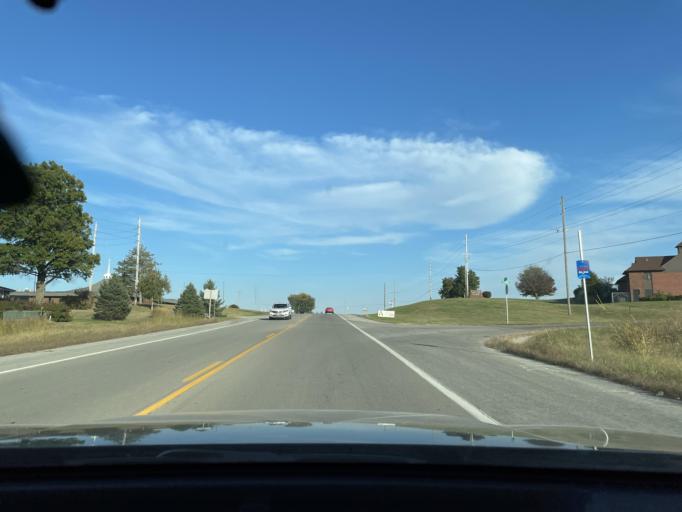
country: US
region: Missouri
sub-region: Buchanan County
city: Saint Joseph
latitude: 39.7554
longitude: -94.7722
